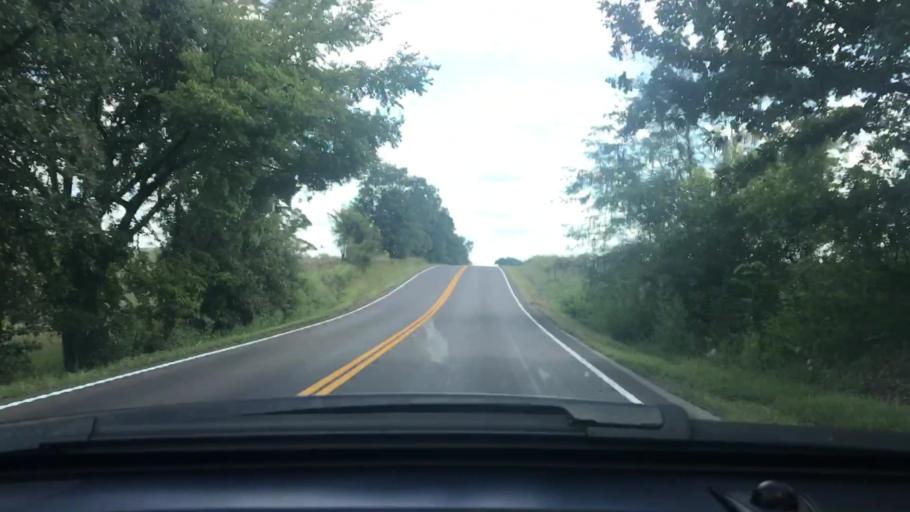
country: US
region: Missouri
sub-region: Wright County
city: Mountain Grove
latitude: 37.2701
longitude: -92.3081
